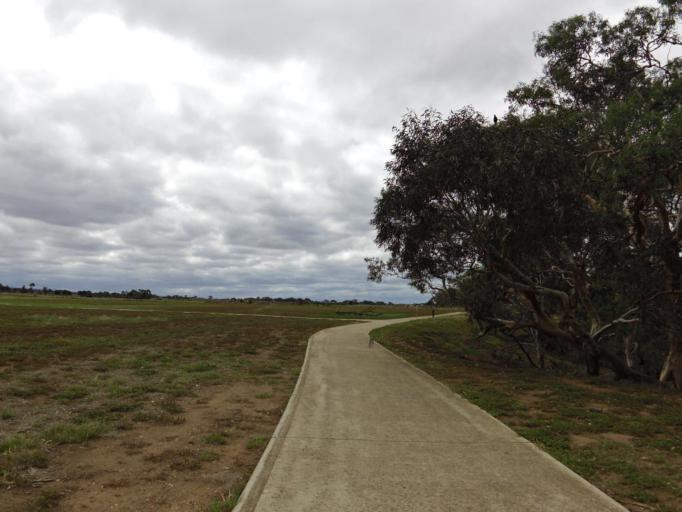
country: AU
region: Victoria
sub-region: Wyndham
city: Tarneit
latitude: -37.8803
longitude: 144.6404
